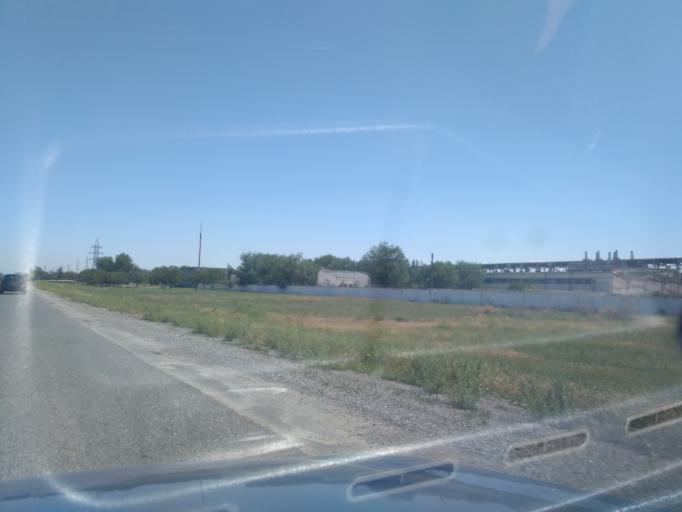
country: TJ
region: Viloyati Sughd
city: Zafarobod
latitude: 40.2165
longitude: 68.8857
